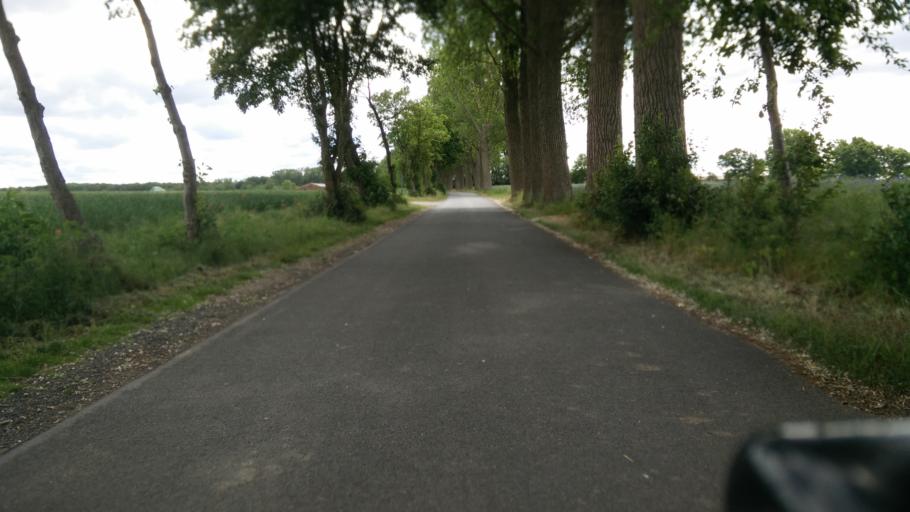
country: DE
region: Lower Saxony
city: Hagenburg
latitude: 52.4491
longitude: 9.3667
